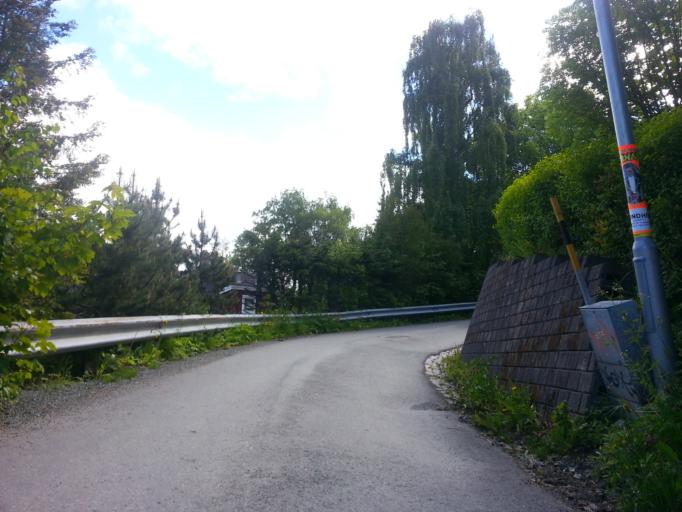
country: NO
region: Sor-Trondelag
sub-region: Trondheim
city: Trondheim
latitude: 63.4132
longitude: 10.3798
